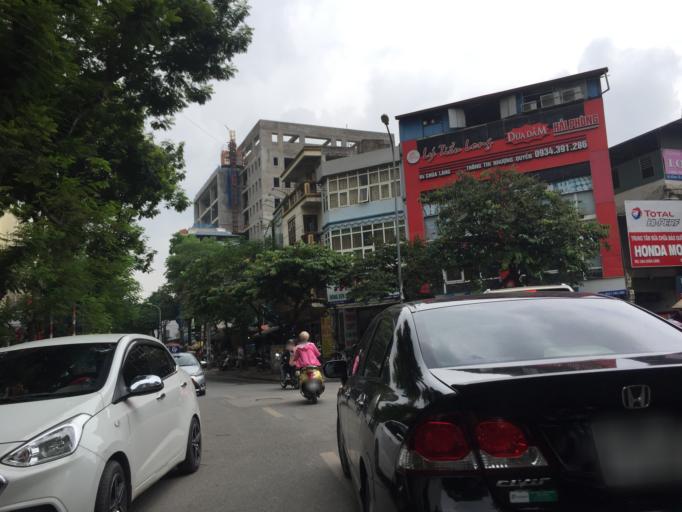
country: VN
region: Ha Noi
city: Cau Giay
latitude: 21.0235
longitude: 105.8055
